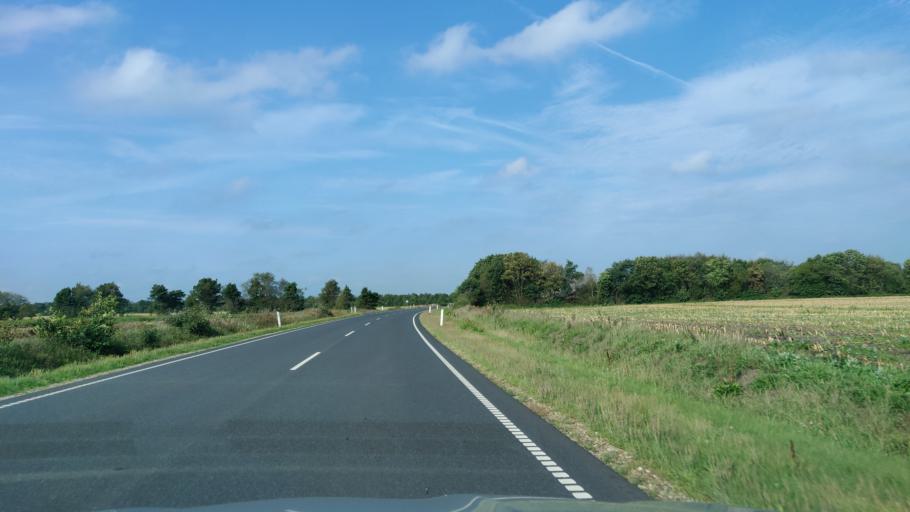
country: DK
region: Central Jutland
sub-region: Herning Kommune
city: Sunds
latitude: 56.2664
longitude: 8.9929
